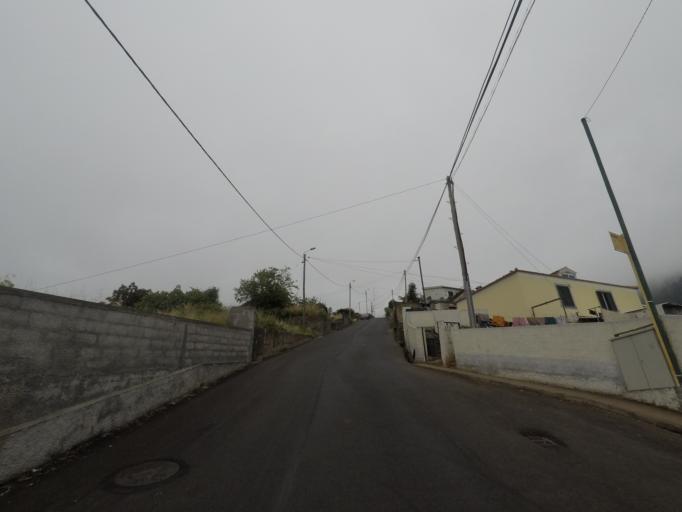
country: PT
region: Madeira
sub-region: Camara de Lobos
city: Curral das Freiras
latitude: 32.6803
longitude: -16.9466
